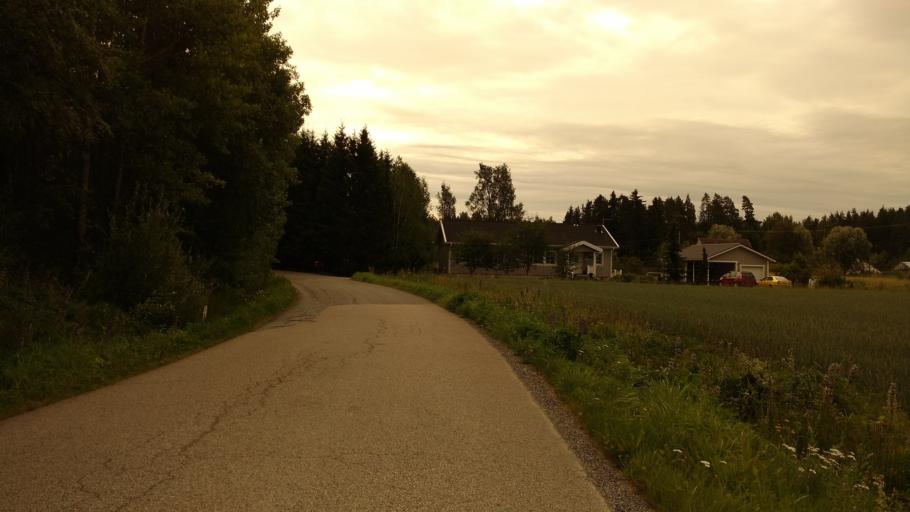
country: FI
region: Varsinais-Suomi
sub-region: Turku
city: Piikkioe
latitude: 60.4365
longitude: 22.4455
